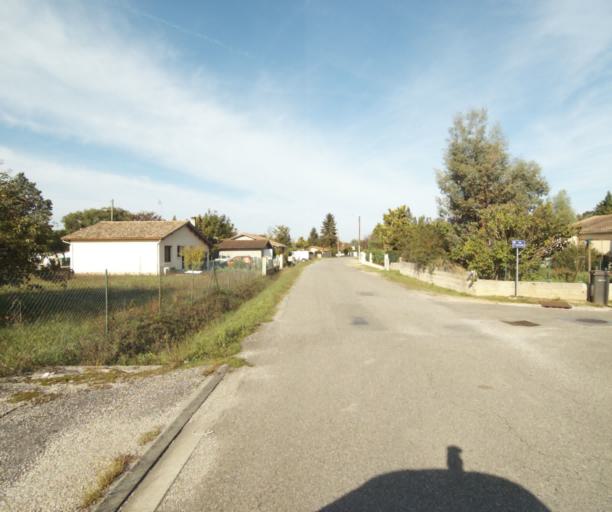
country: FR
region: Midi-Pyrenees
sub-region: Departement du Tarn-et-Garonne
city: Nohic
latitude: 43.9089
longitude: 1.4481
